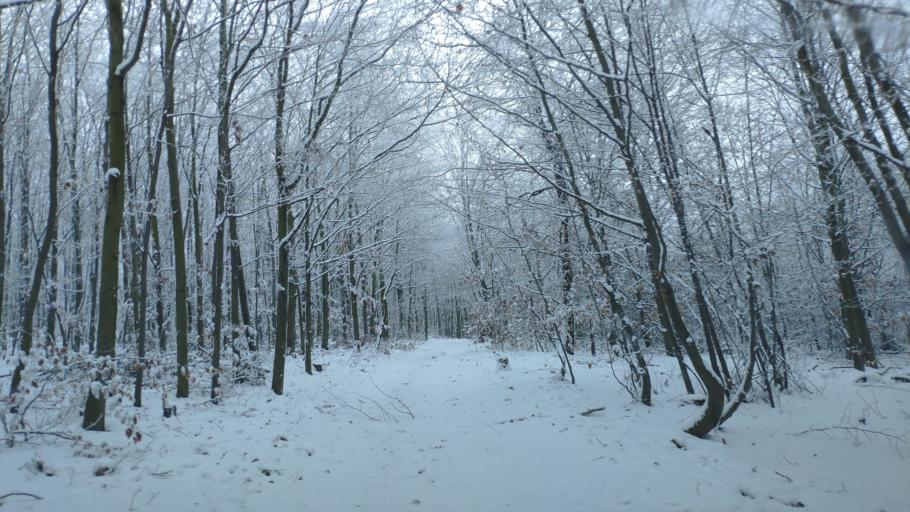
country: SK
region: Kosicky
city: Kosice
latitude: 48.6560
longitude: 21.1817
